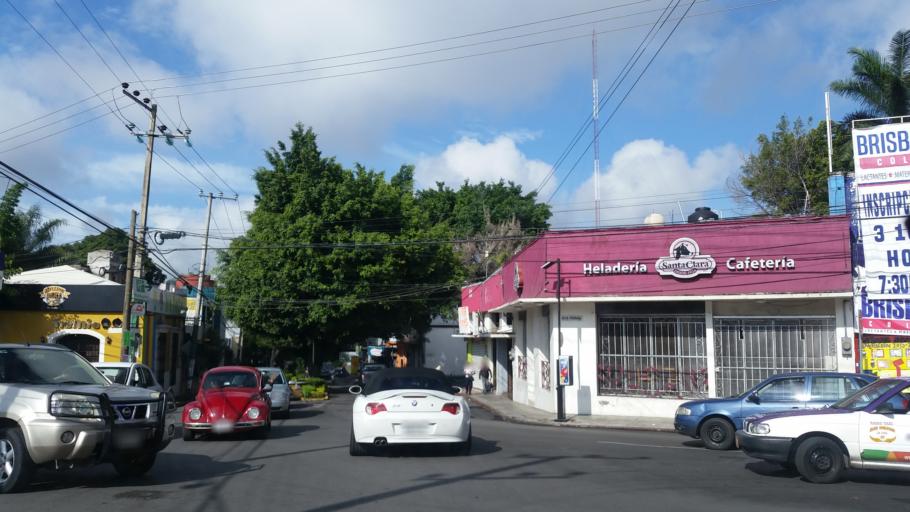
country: MX
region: Morelos
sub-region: Cuernavaca
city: Cuernavaca
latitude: 18.9178
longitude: -99.2194
